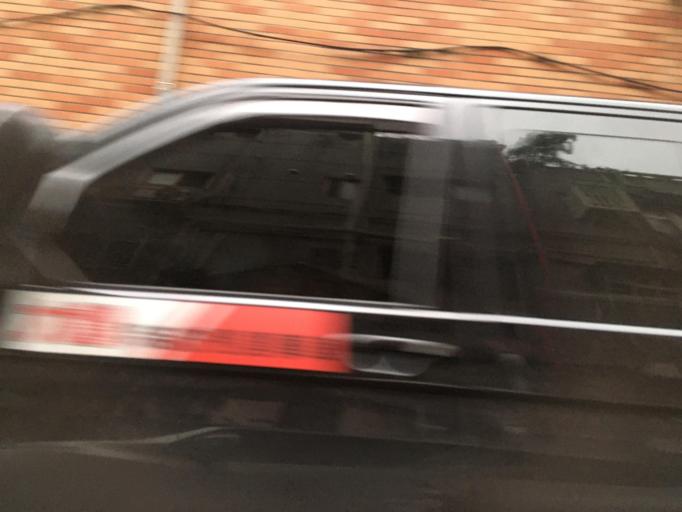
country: TW
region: Taipei
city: Taipei
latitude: 25.0723
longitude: 121.5150
